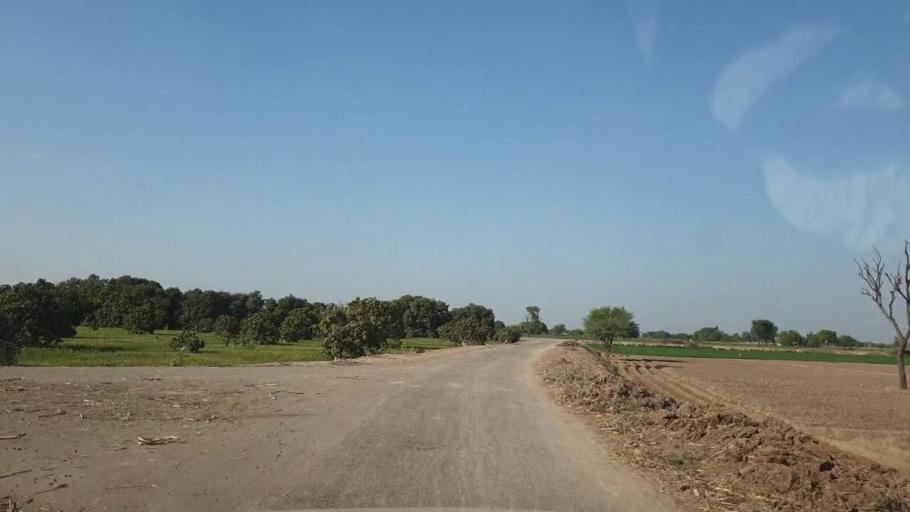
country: PK
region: Sindh
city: Tando Allahyar
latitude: 25.4886
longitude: 68.6556
